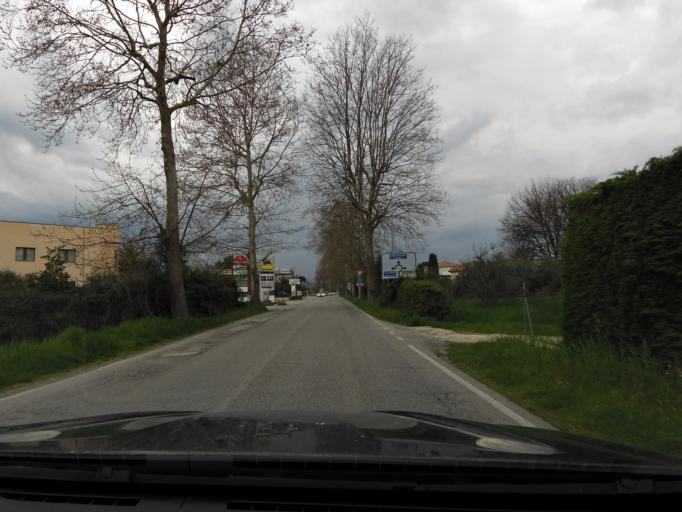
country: IT
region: The Marches
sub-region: Provincia di Ancona
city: Villa Musone
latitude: 43.4464
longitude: 13.6100
